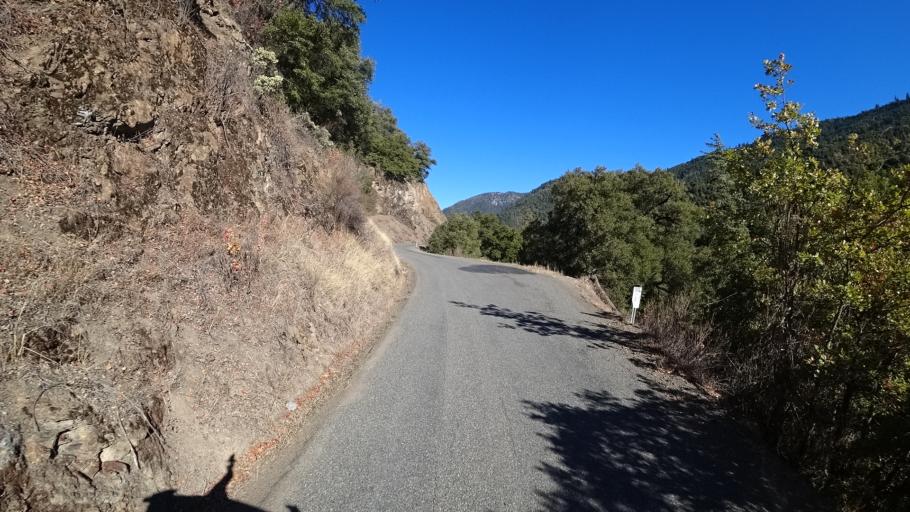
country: US
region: California
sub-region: Humboldt County
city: Willow Creek
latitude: 41.2729
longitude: -123.2952
